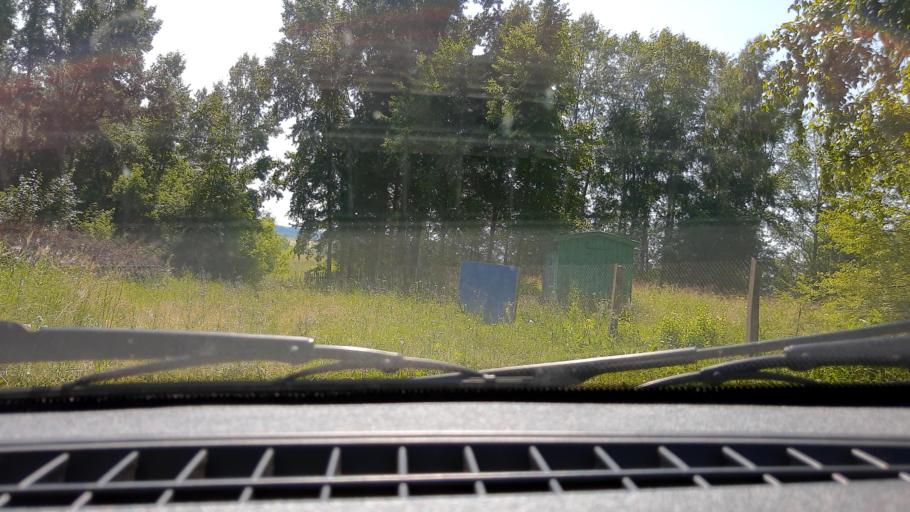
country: RU
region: Bashkortostan
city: Kushnarenkovo
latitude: 55.0730
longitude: 55.1649
